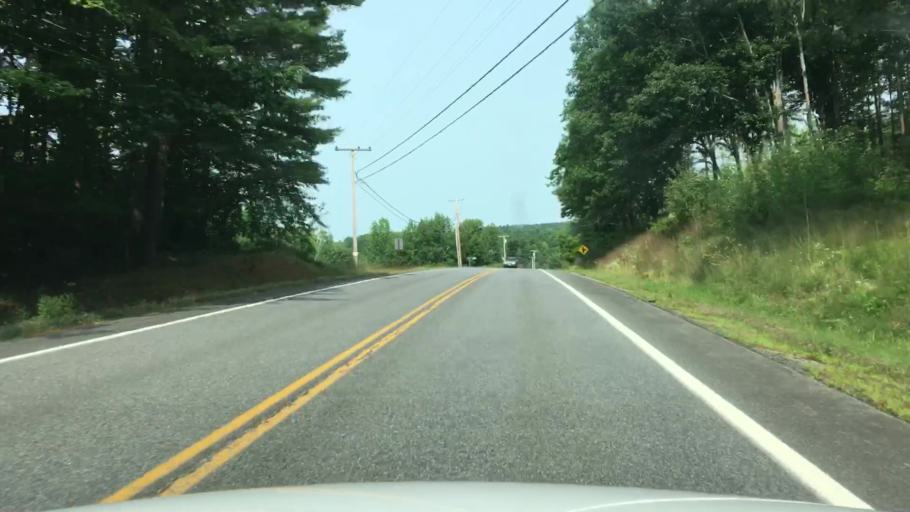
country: US
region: Maine
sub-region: Kennebec County
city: Winthrop
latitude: 44.3355
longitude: -70.0138
